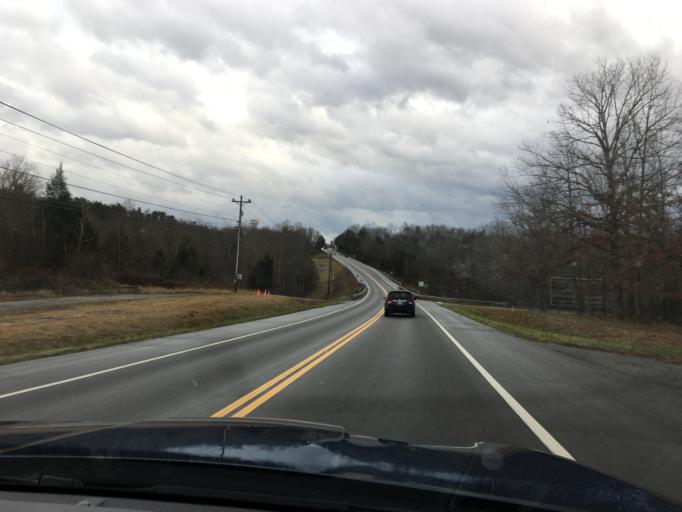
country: US
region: Tennessee
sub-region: Cumberland County
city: Crossville
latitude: 35.9130
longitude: -84.9929
